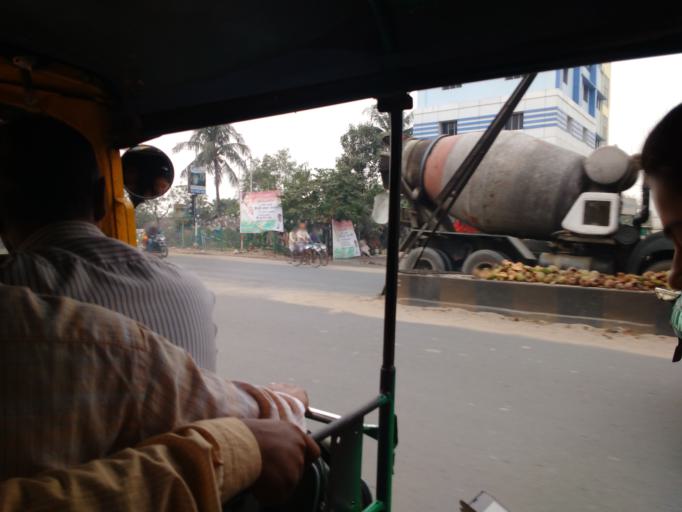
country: IN
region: West Bengal
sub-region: North 24 Parganas
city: Baranagar
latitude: 22.6520
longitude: 88.3726
